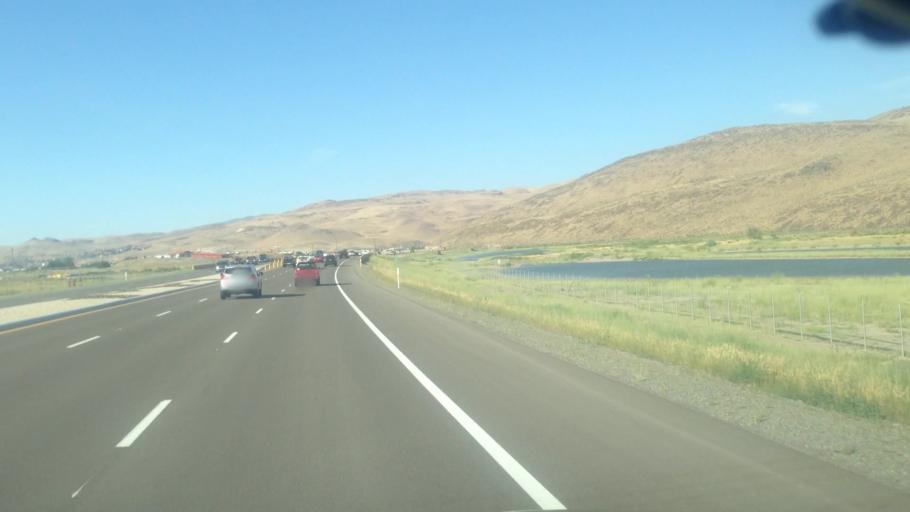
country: US
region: Nevada
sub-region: Washoe County
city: Sparks
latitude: 39.5024
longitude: -119.7254
